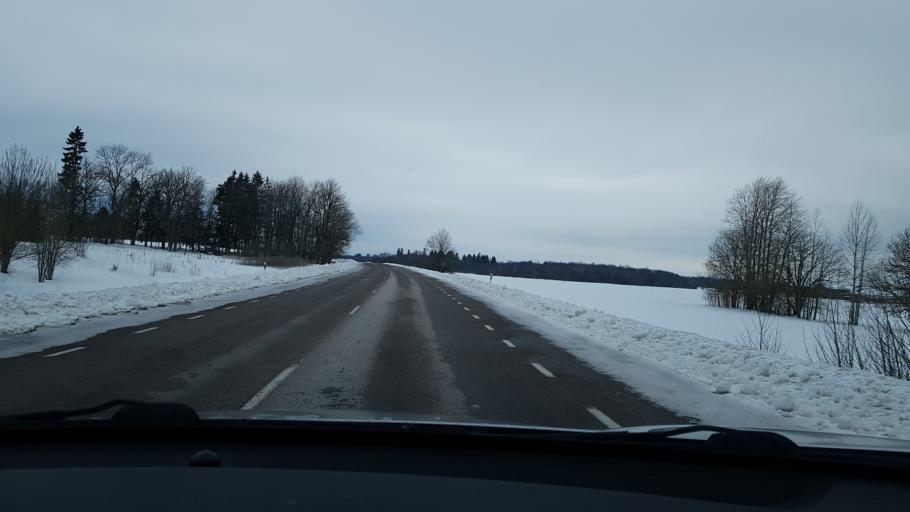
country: EE
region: Jaervamaa
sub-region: Jaerva-Jaani vald
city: Jarva-Jaani
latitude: 58.9040
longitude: 25.8131
